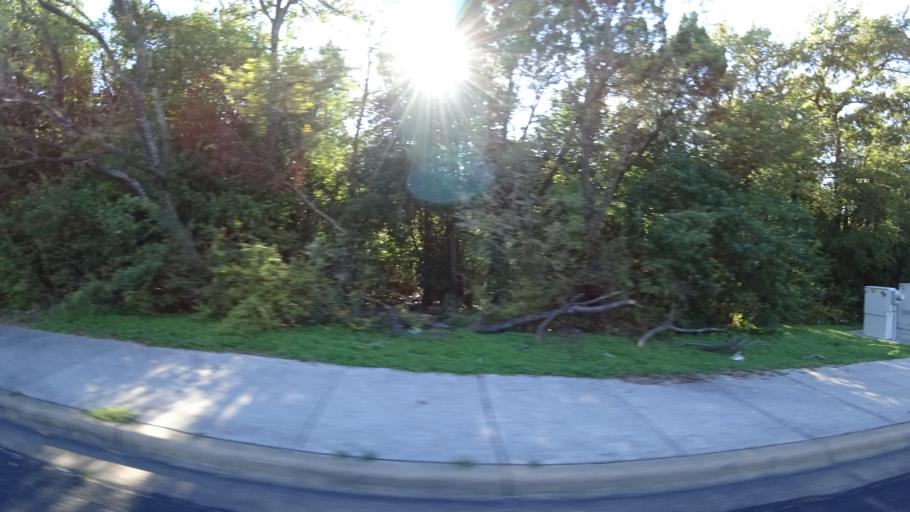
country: US
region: Texas
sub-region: Travis County
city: Austin
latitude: 30.2217
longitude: -97.7214
